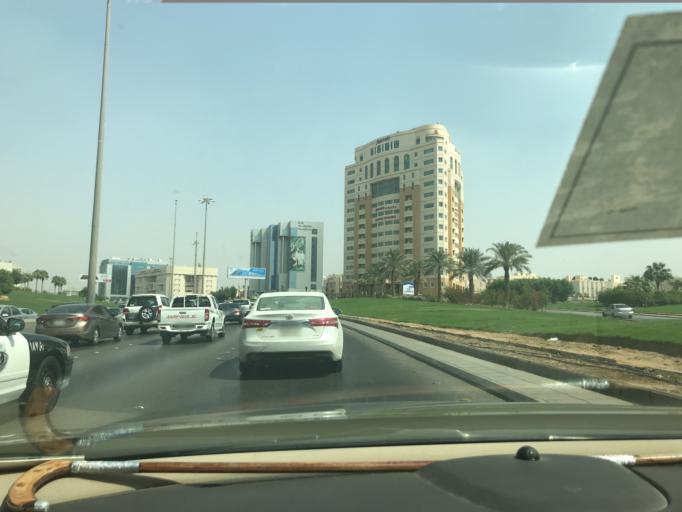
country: SA
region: Ar Riyad
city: Riyadh
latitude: 24.6877
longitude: 46.7114
